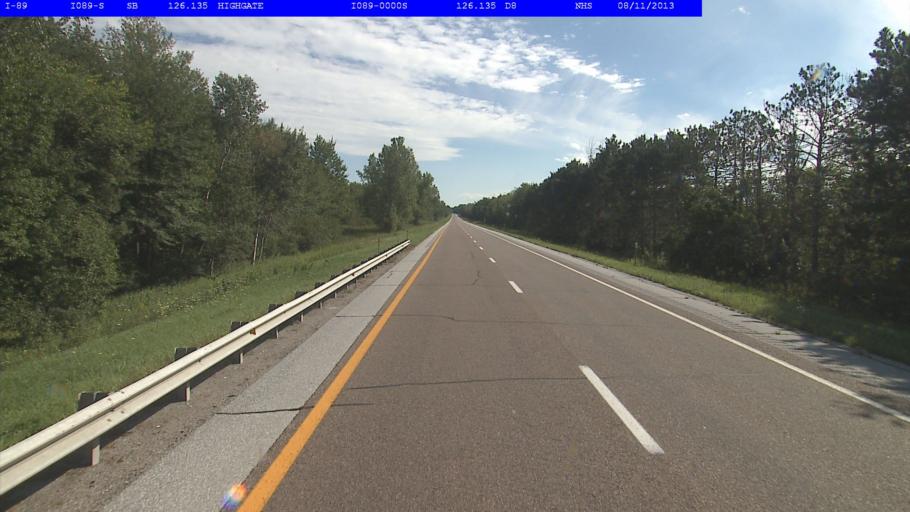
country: US
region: Vermont
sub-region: Franklin County
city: Swanton
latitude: 44.9609
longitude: -73.1087
